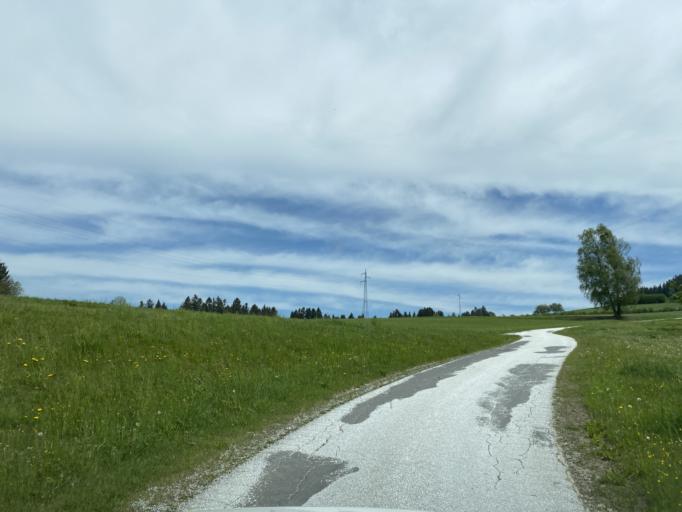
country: AT
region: Styria
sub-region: Politischer Bezirk Weiz
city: Gschaid bei Birkfeld
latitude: 47.3547
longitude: 15.7156
